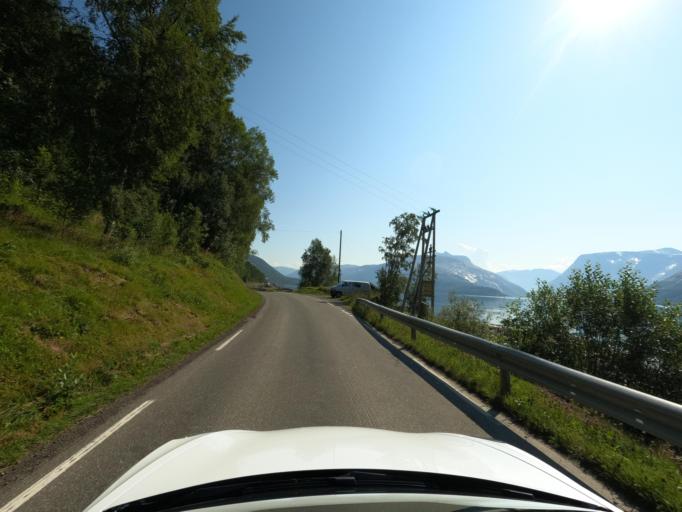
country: NO
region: Nordland
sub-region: Narvik
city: Narvik
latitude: 68.2890
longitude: 17.3648
